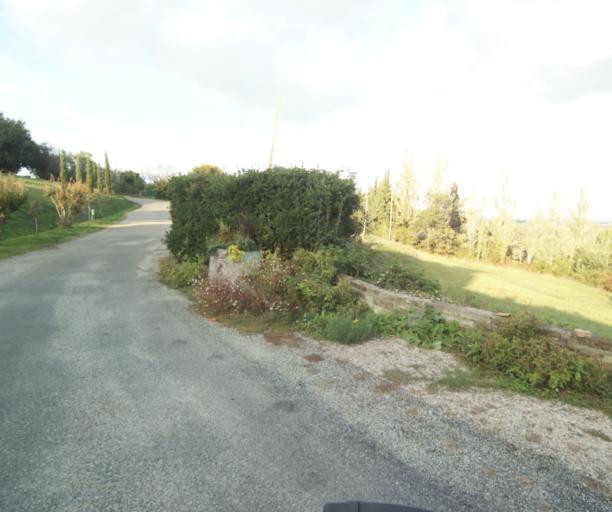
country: FR
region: Midi-Pyrenees
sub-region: Departement de la Haute-Garonne
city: Launac
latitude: 43.8217
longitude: 1.1180
